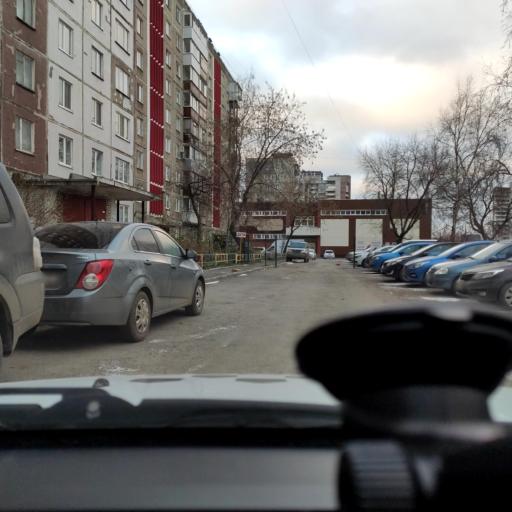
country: RU
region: Perm
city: Kondratovo
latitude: 57.9970
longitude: 56.1433
